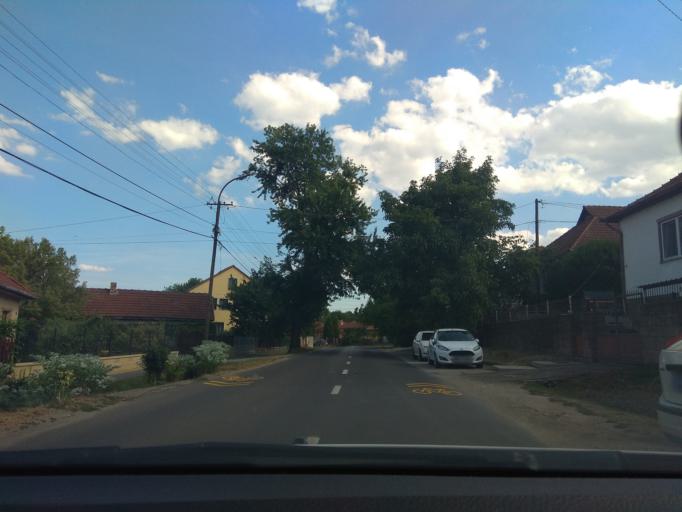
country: HU
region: Borsod-Abauj-Zemplen
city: Miskolc
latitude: 48.0549
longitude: 20.7905
